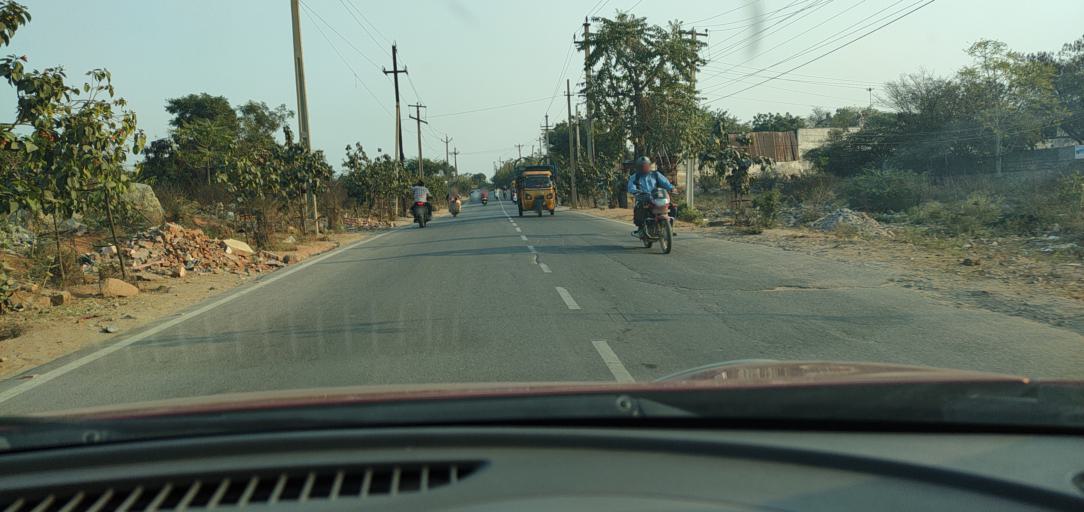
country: IN
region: Telangana
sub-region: Rangareddi
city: Uppal Kalan
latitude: 17.4326
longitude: 78.5780
